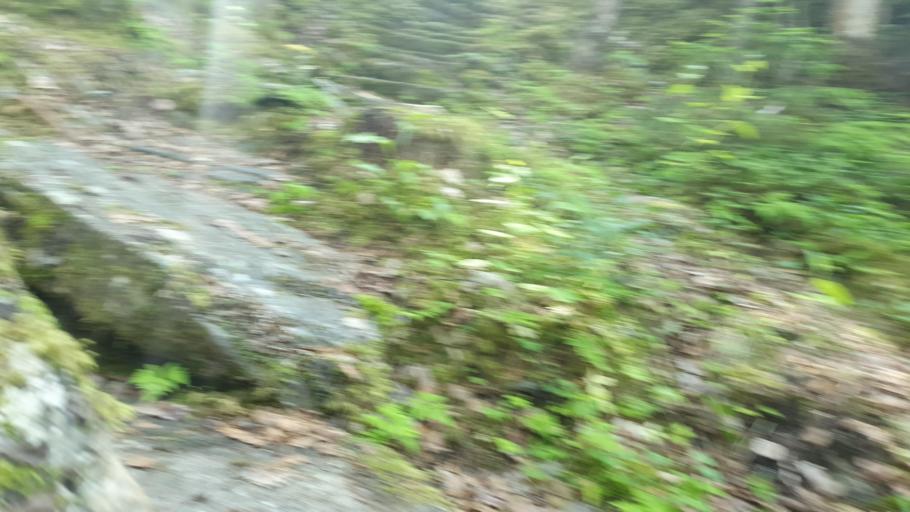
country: NO
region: Sor-Trondelag
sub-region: Malvik
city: Hommelvik
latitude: 63.4111
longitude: 10.7889
